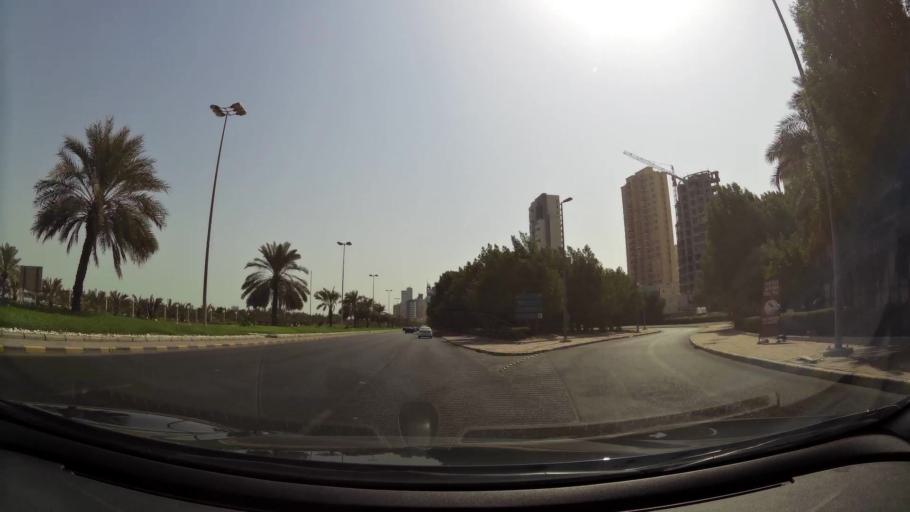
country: KW
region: Al Asimah
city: Ad Dasmah
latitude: 29.3581
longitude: 48.0259
